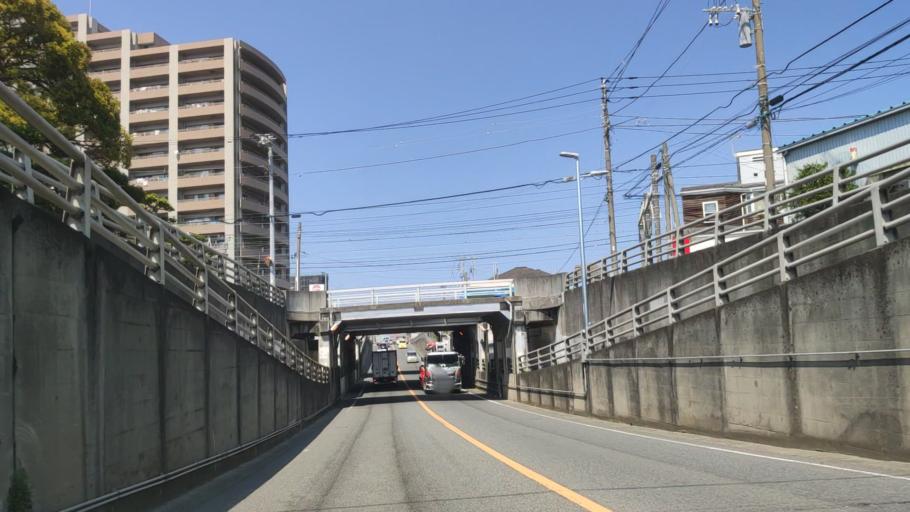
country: JP
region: Kanagawa
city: Chigasaki
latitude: 35.3305
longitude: 139.3770
